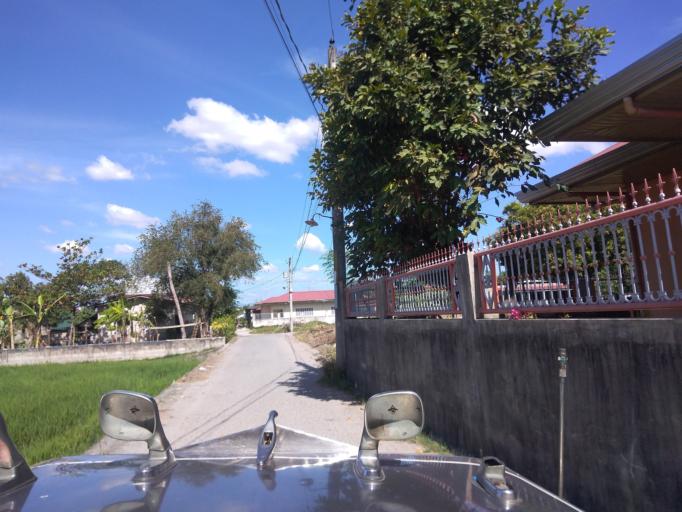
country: PH
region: Central Luzon
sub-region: Province of Pampanga
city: Santa Rita
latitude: 14.9939
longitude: 120.6106
